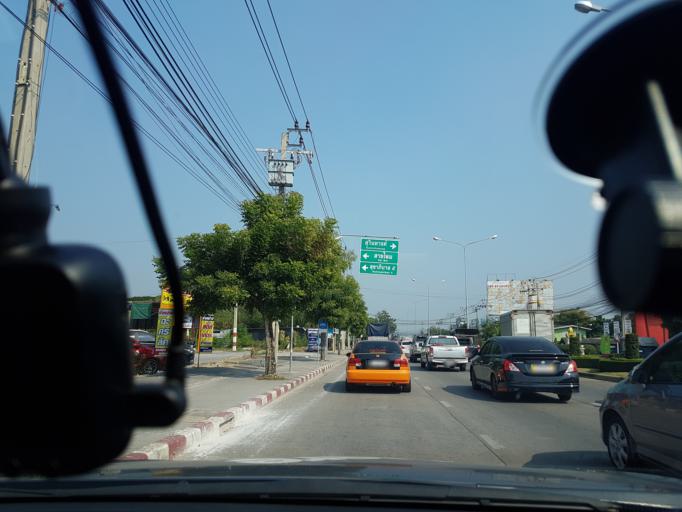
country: TH
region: Bangkok
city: Khlong Sam Wa
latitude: 13.8618
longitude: 100.7203
